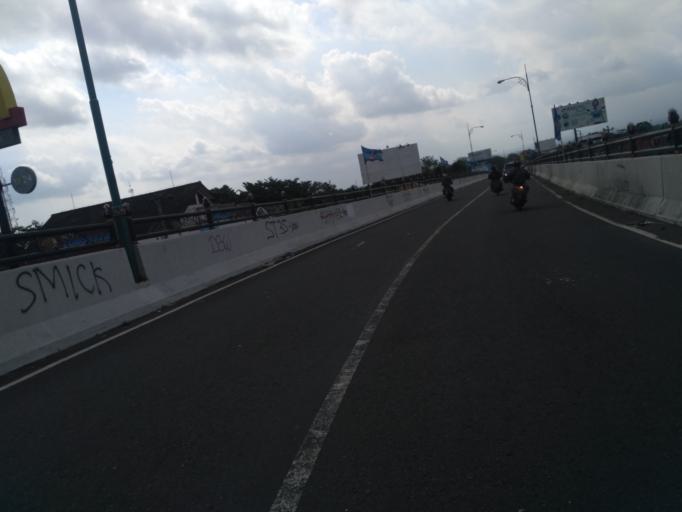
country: ID
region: Daerah Istimewa Yogyakarta
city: Melati
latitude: -7.7487
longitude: 110.3624
